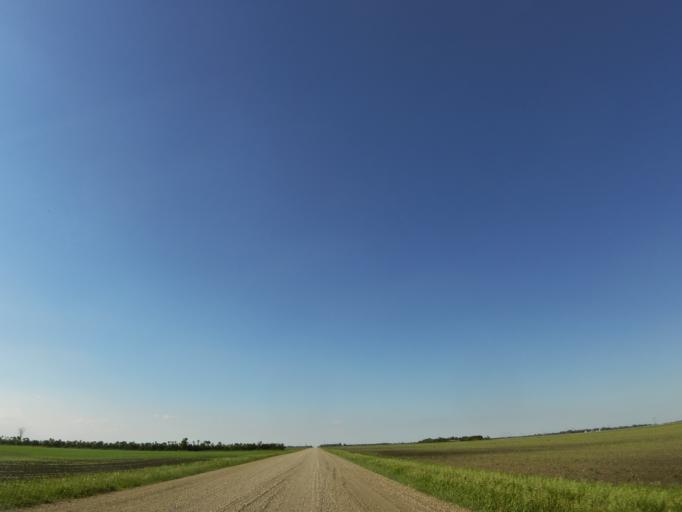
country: US
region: North Dakota
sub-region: Walsh County
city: Grafton
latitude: 48.4016
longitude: -97.2777
